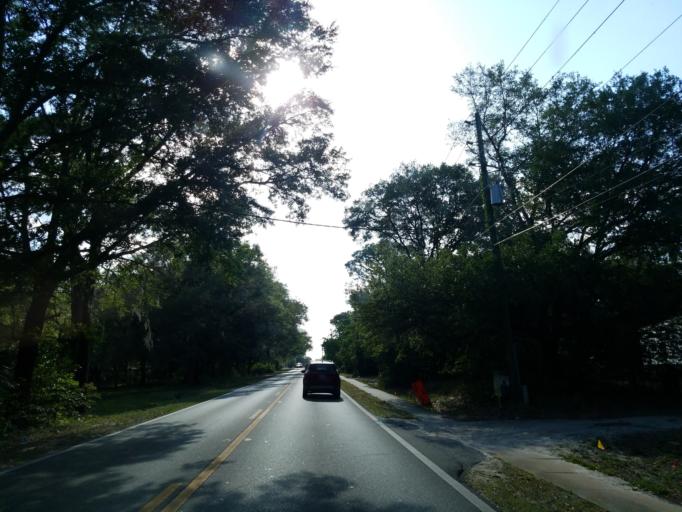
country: US
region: Florida
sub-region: Lake County
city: Fruitland Park
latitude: 28.8616
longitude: -81.9175
